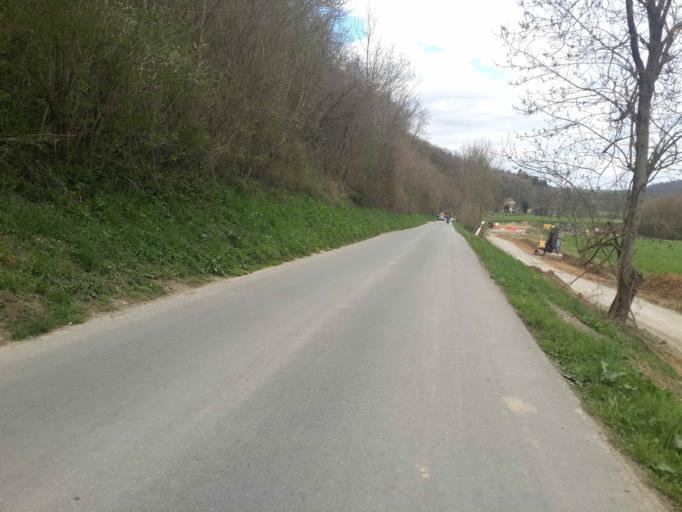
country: DE
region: Baden-Wuerttemberg
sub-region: Regierungsbezirk Stuttgart
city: Oedheim
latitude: 49.2669
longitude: 9.2175
